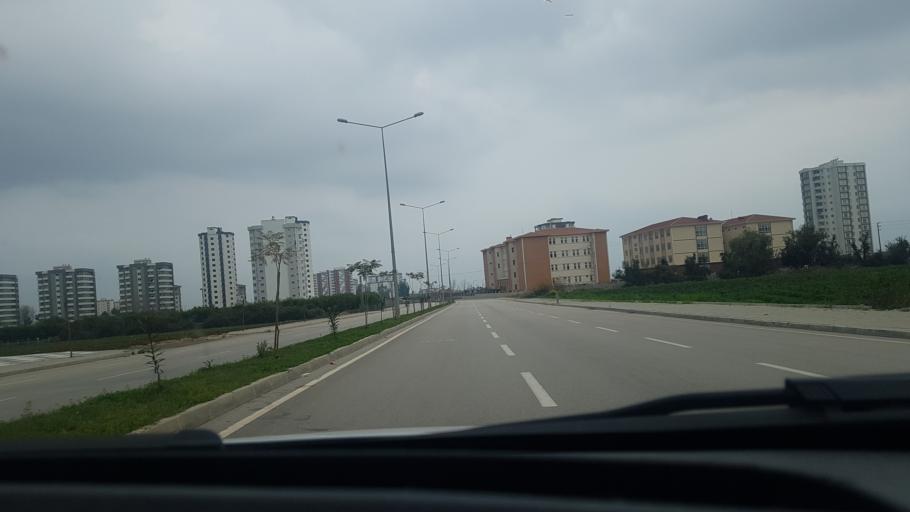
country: TR
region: Adana
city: Seyhan
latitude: 37.0134
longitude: 35.2571
